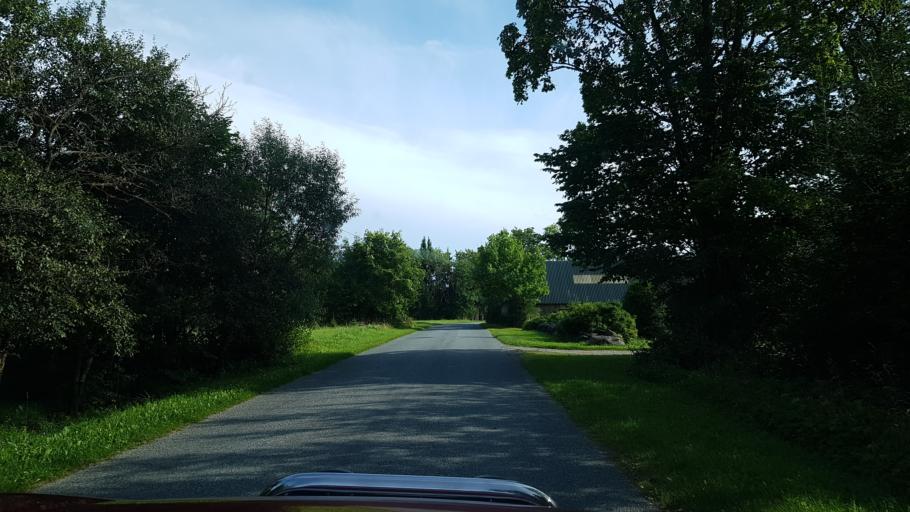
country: EE
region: Laeaene
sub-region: Lihula vald
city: Lihula
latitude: 58.4456
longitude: 24.0024
